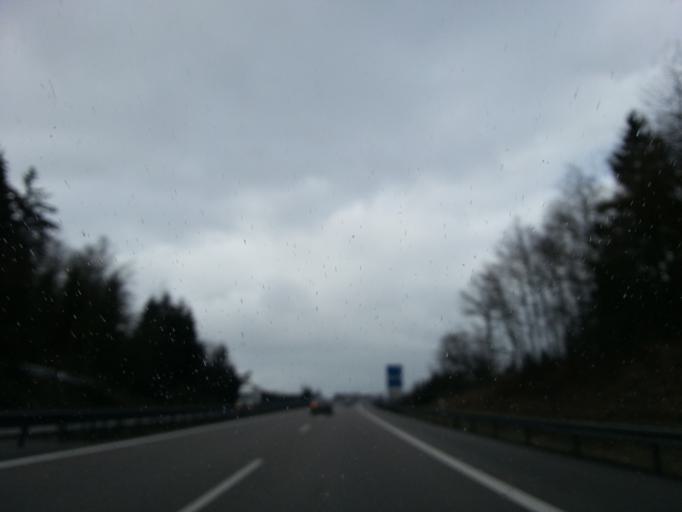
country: DE
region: Bavaria
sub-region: Upper Palatinate
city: Velburg
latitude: 49.2598
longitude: 11.6068
